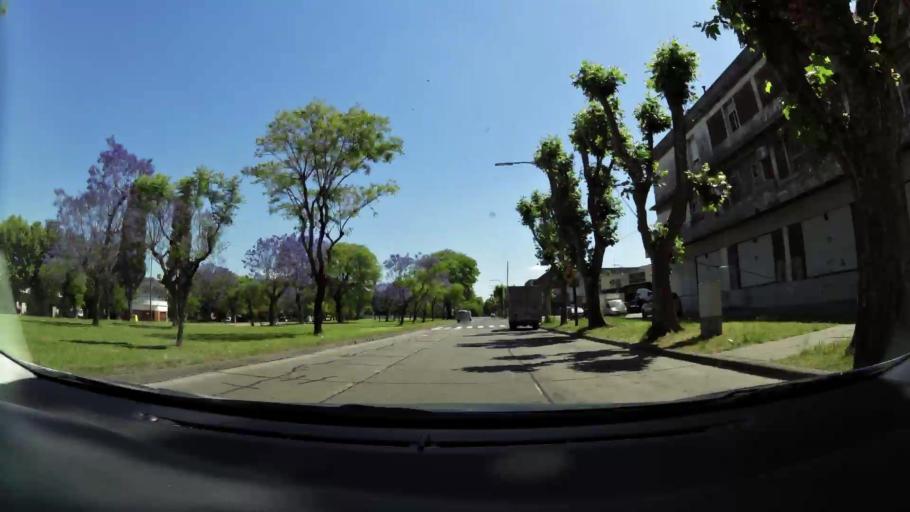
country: AR
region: Buenos Aires F.D.
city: Villa Lugano
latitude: -34.6588
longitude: -58.4270
